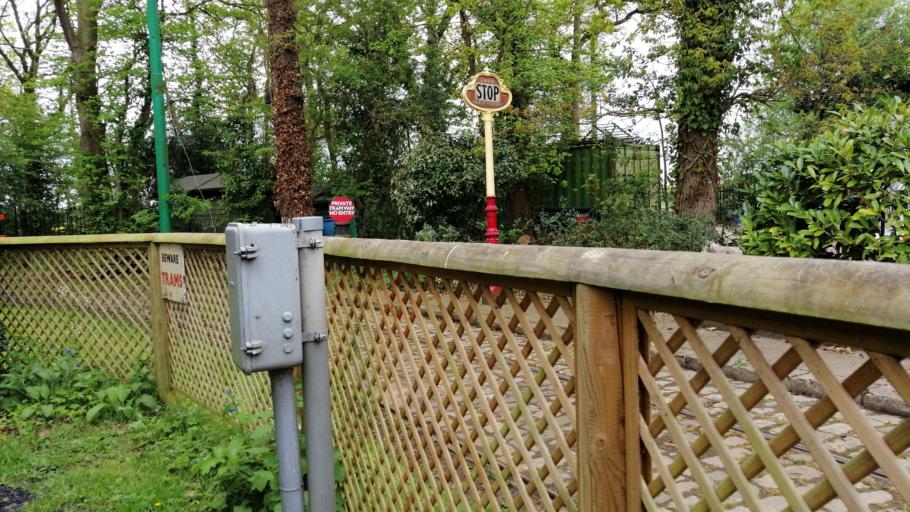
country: GB
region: England
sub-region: Suffolk
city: Kessingland
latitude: 52.4520
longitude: 1.6849
